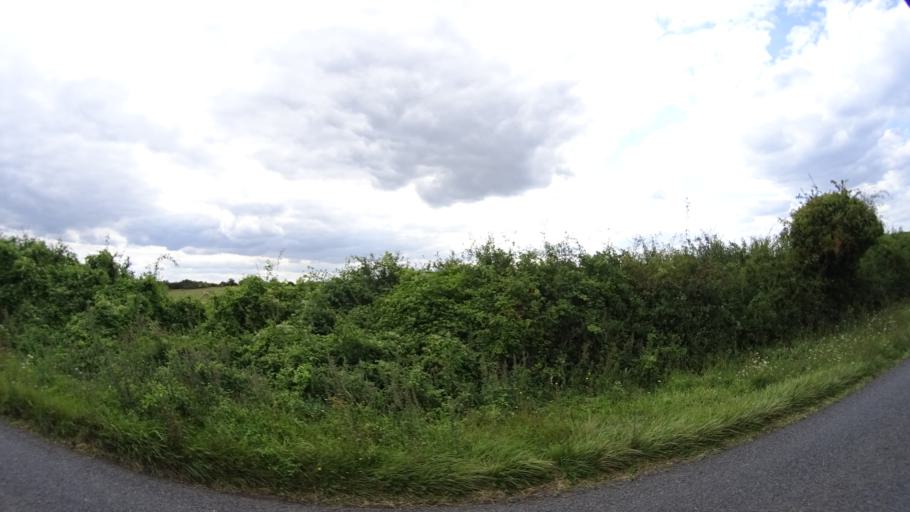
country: GB
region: England
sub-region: Wiltshire
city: Tidworth
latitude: 51.1759
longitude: -1.6391
